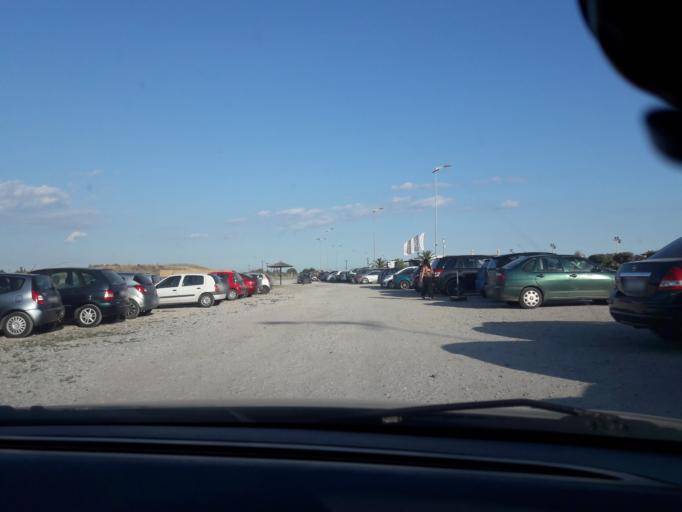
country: GR
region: Central Macedonia
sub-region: Nomos Chalkidikis
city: Nea Kallikrateia
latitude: 40.3253
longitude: 23.0203
